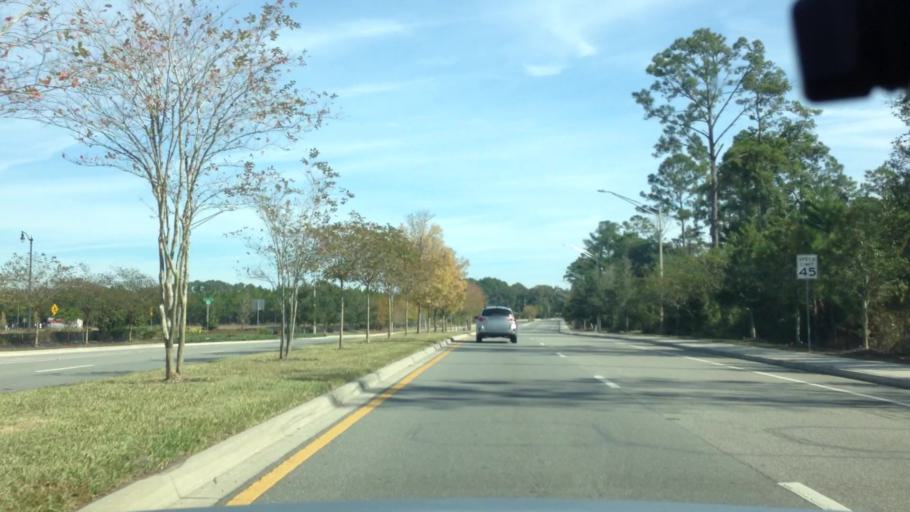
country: US
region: Florida
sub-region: Nassau County
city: Yulee
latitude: 30.4898
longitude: -81.6316
